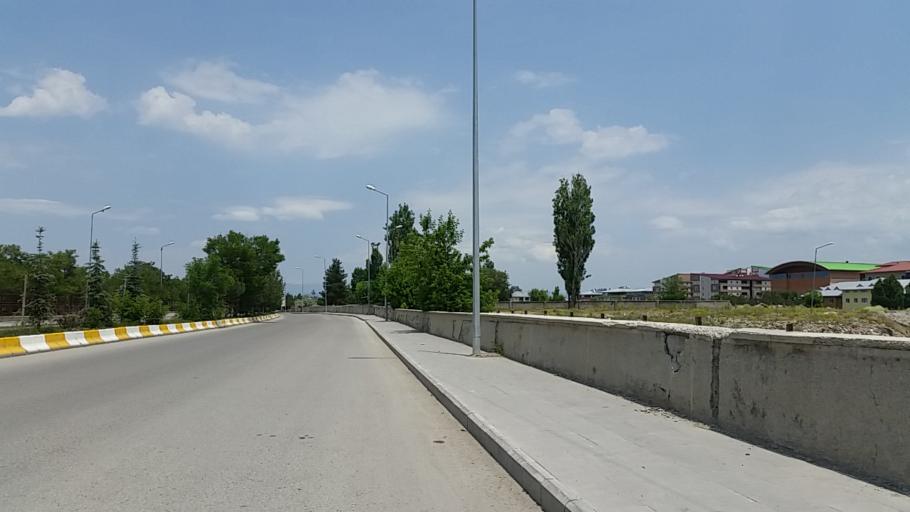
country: TR
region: Agri
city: Agri
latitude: 39.7165
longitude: 43.0273
